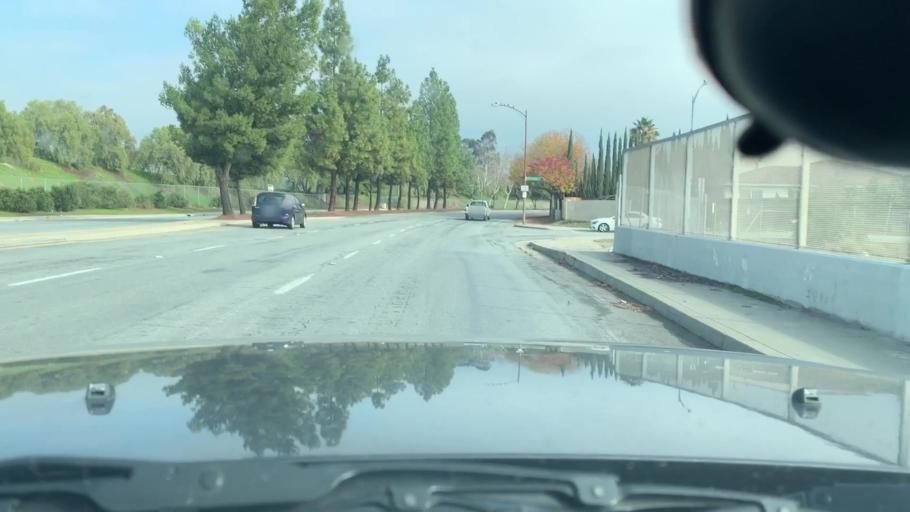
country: US
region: California
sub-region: Santa Clara County
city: Alum Rock
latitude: 37.3328
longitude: -121.8102
